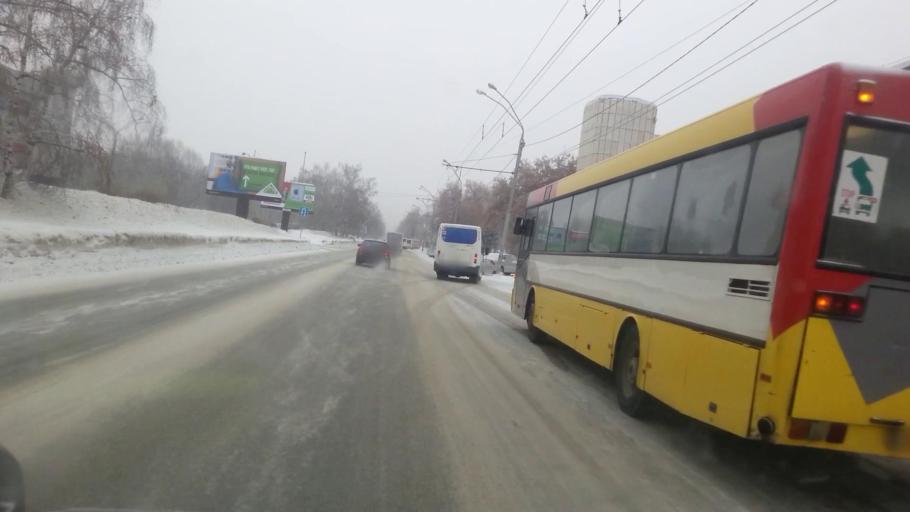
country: RU
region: Altai Krai
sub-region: Gorod Barnaulskiy
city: Barnaul
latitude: 53.3821
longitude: 83.7395
